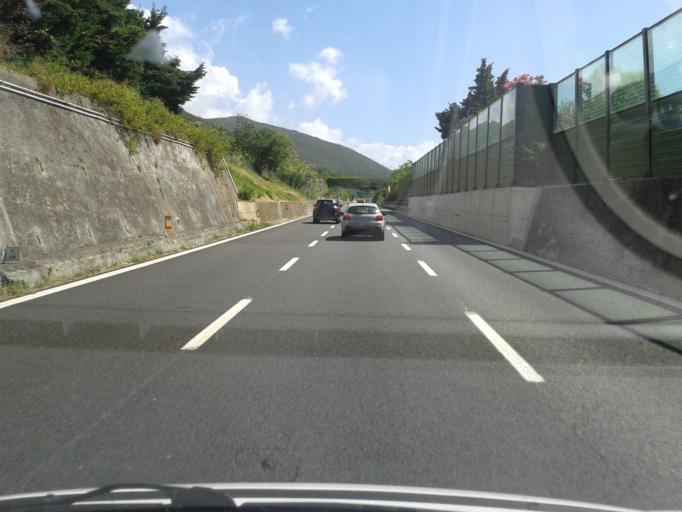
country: IT
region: Liguria
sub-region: Provincia di Savona
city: Varazze
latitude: 44.3630
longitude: 8.5939
